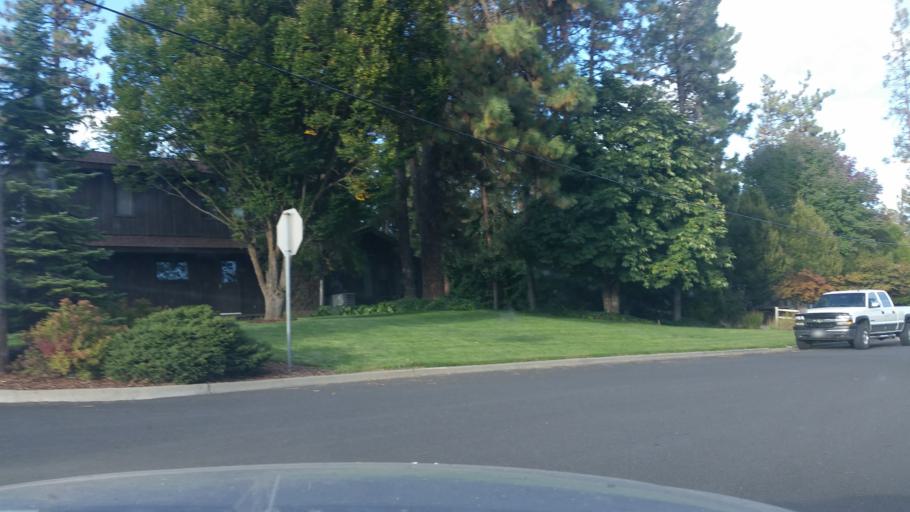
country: US
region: Washington
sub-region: Spokane County
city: Cheney
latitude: 47.4834
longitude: -117.5899
